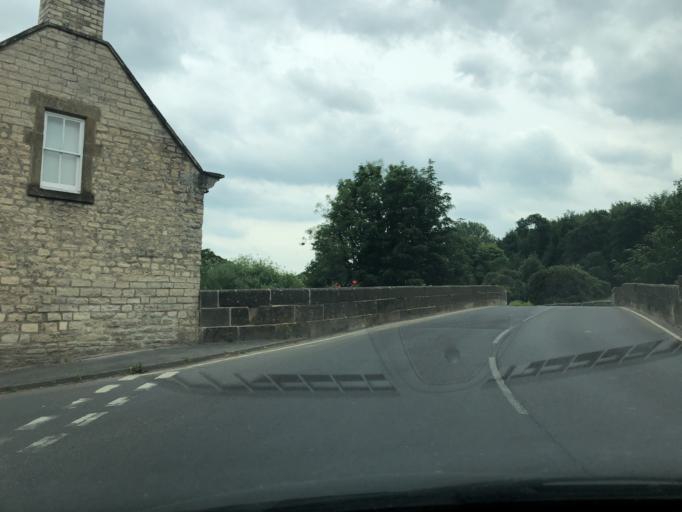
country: GB
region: England
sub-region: North Yorkshire
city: Helmsley
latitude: 54.2445
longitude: -1.0593
